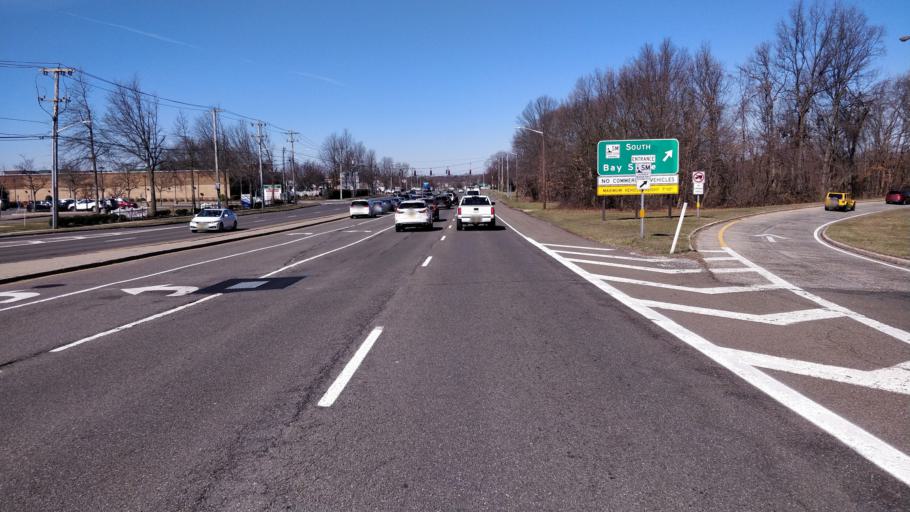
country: US
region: New York
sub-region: Suffolk County
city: Commack
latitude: 40.8401
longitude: -73.2823
